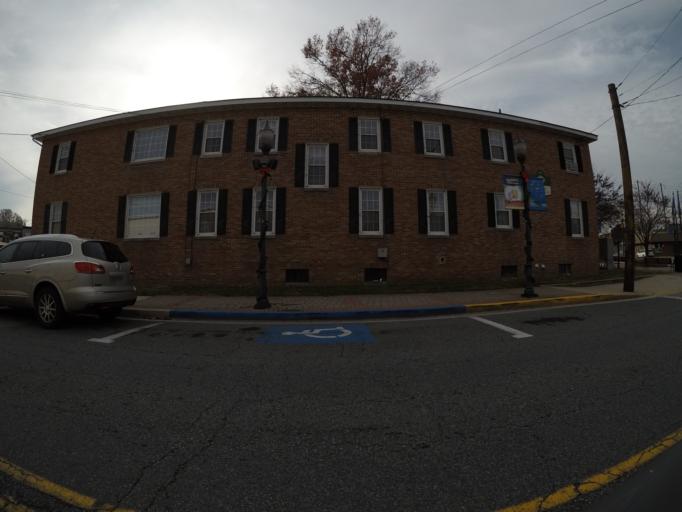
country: US
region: Maryland
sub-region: Harford County
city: Havre de Grace
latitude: 39.5516
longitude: -76.0913
